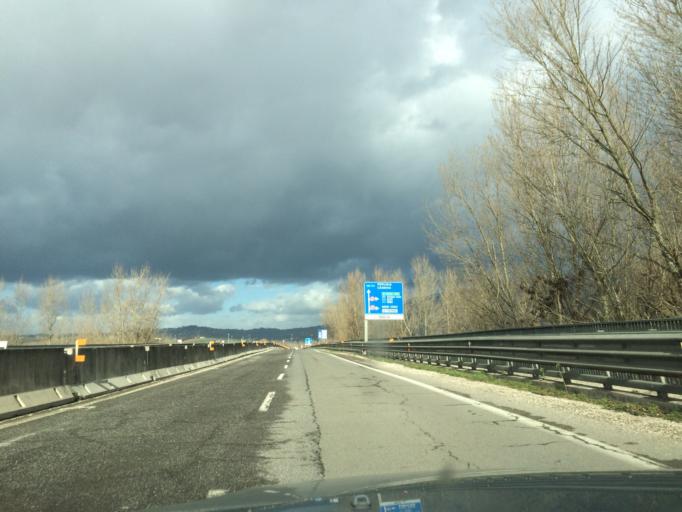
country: IT
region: Umbria
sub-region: Provincia di Terni
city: Terni
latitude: 42.5568
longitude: 12.5832
